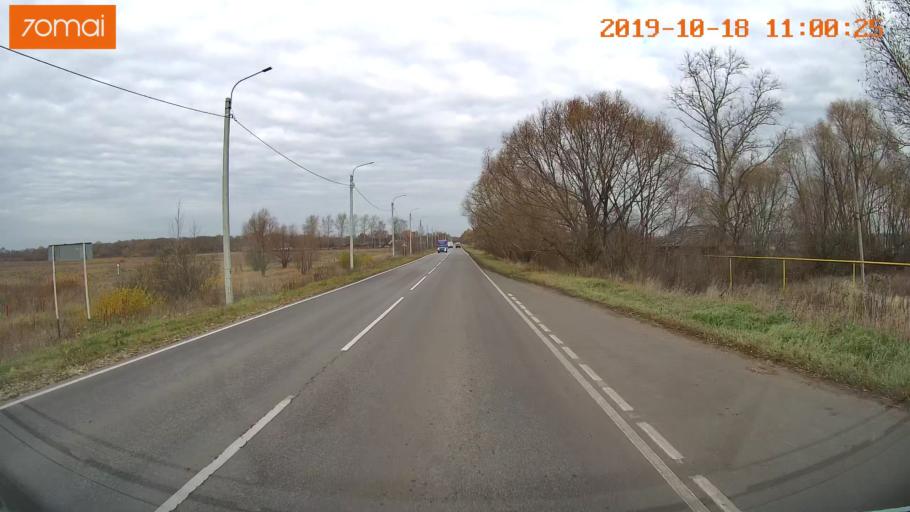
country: RU
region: Tula
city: Yepifan'
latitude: 53.8428
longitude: 38.5527
